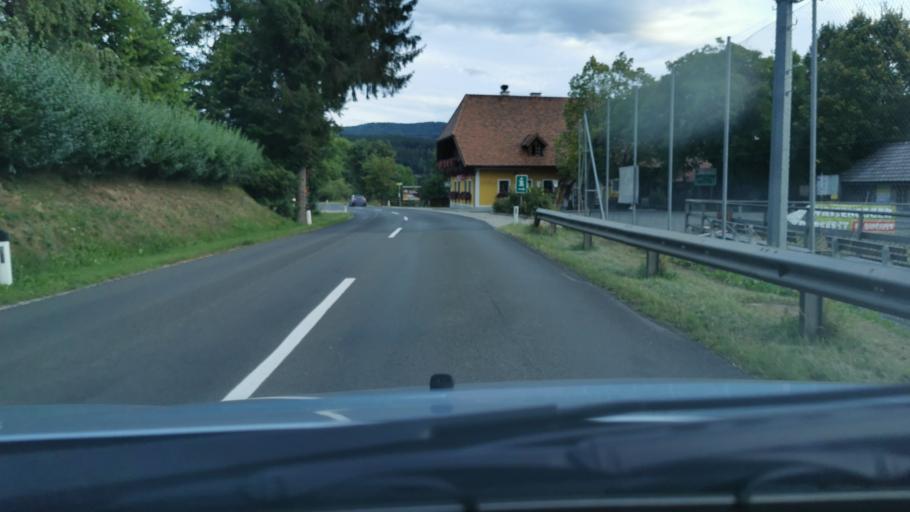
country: AT
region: Styria
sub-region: Politischer Bezirk Weiz
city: Birkfeld
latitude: 47.3826
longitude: 15.6779
